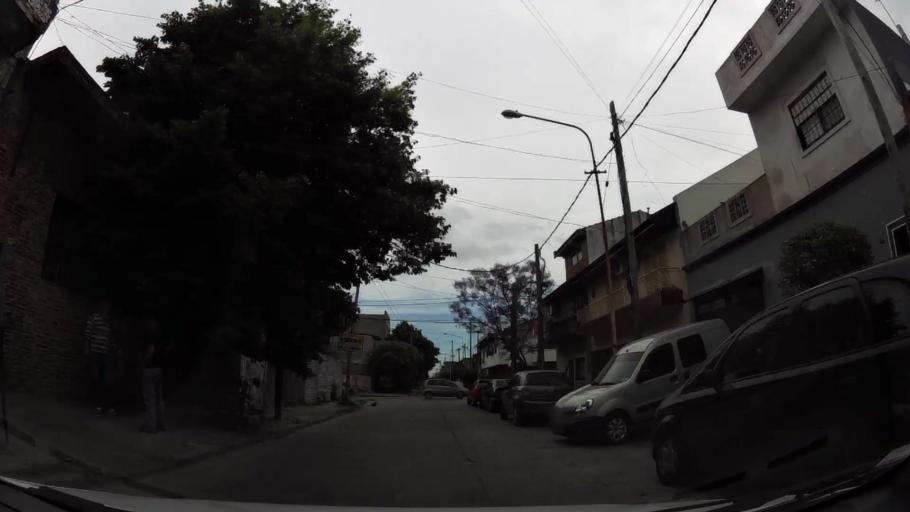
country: AR
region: Buenos Aires
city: San Justo
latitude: -34.6637
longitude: -58.5289
